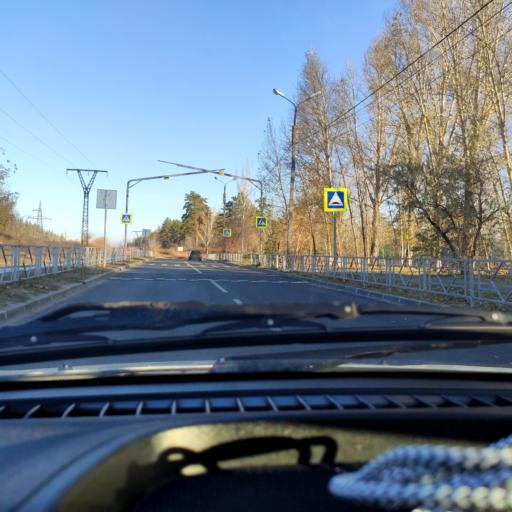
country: RU
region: Samara
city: Zhigulevsk
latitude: 53.4824
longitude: 49.4546
